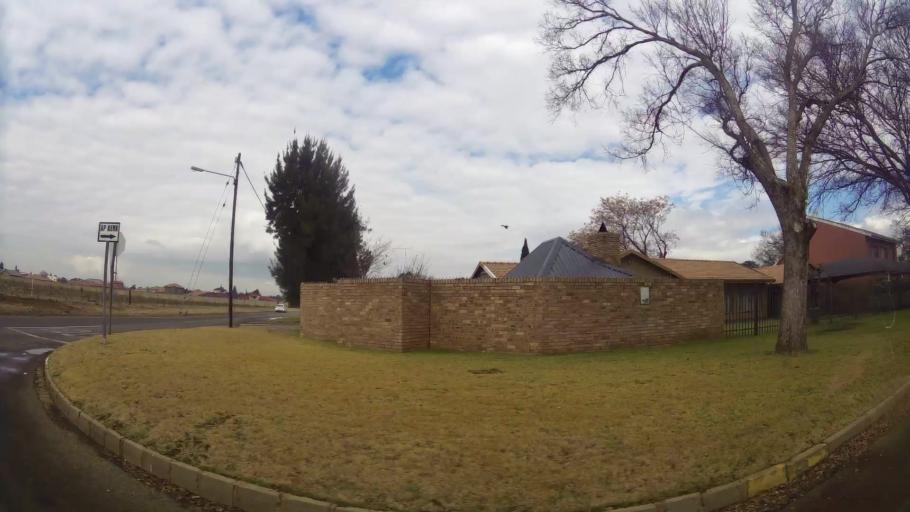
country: ZA
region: Gauteng
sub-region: Sedibeng District Municipality
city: Vereeniging
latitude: -26.6452
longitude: 27.9893
